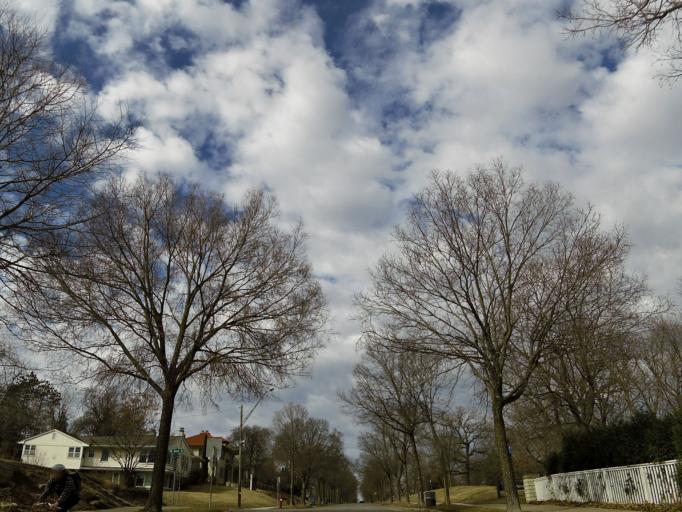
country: US
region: Minnesota
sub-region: Hennepin County
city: Saint Louis Park
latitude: 44.9193
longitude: -93.3151
